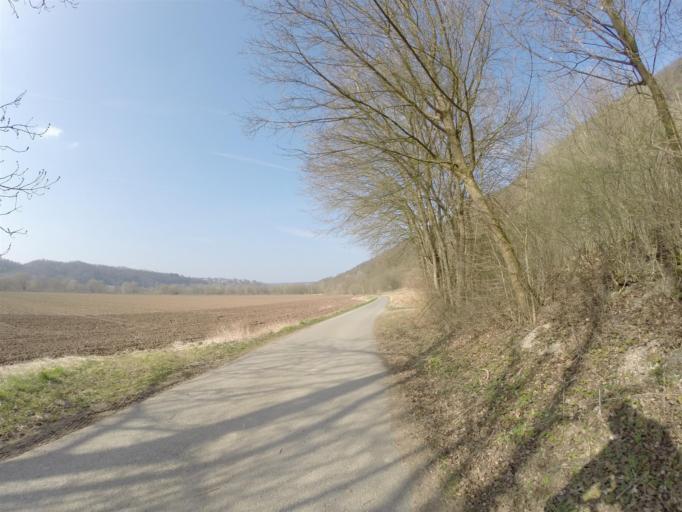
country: DE
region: Thuringia
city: Golmsdorf
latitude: 50.9860
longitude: 11.6740
